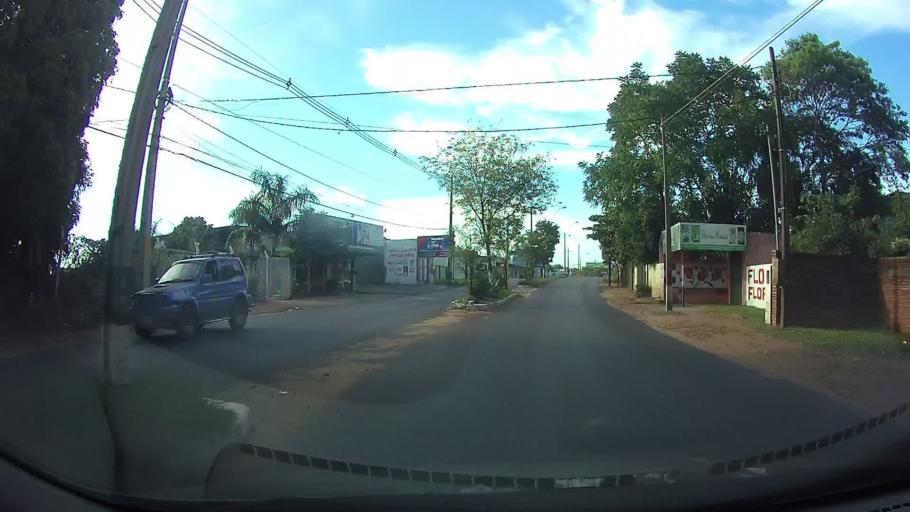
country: PY
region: Central
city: Villa Elisa
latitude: -25.3943
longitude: -57.5816
